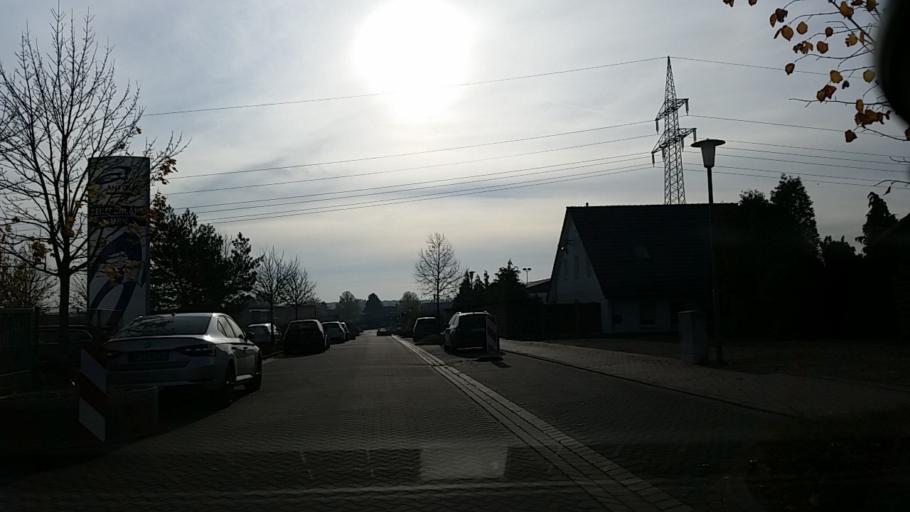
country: DE
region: Lower Saxony
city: Weyhausen
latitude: 52.4653
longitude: 10.7237
